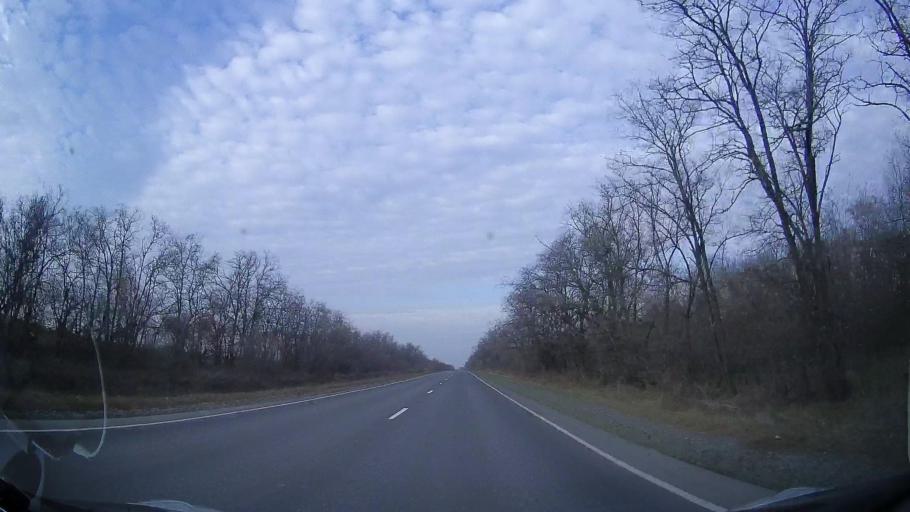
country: RU
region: Rostov
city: Bagayevskaya
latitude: 47.1240
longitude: 40.2767
